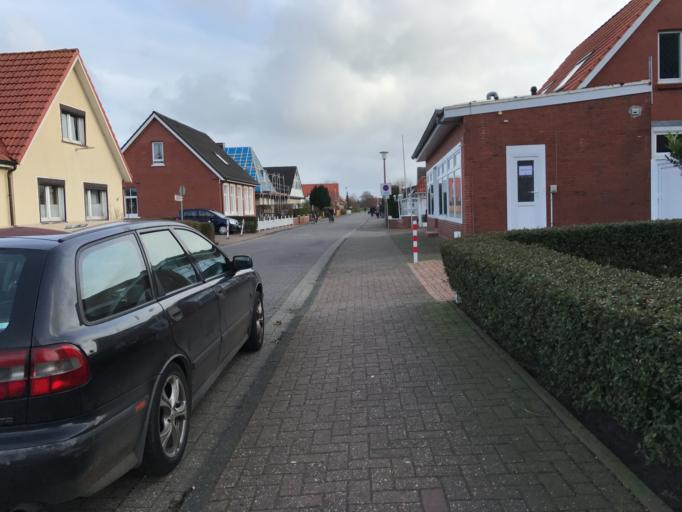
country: DE
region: Lower Saxony
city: Borkum
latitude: 53.5836
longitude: 6.6758
